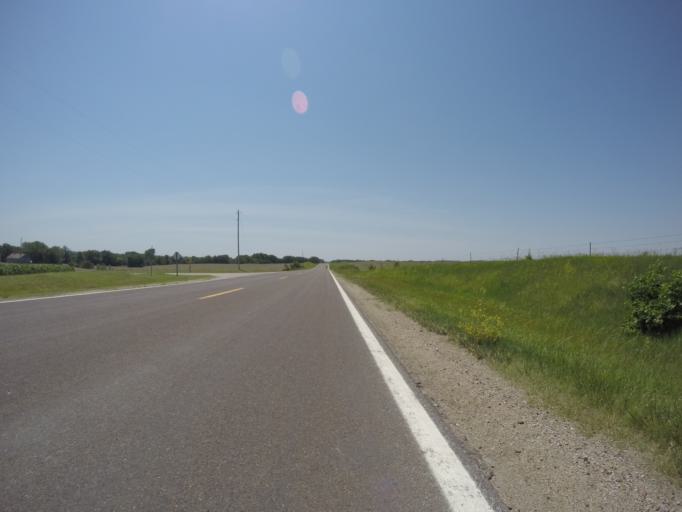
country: US
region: Nebraska
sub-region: Pawnee County
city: Pawnee City
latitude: 40.0142
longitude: -96.0484
